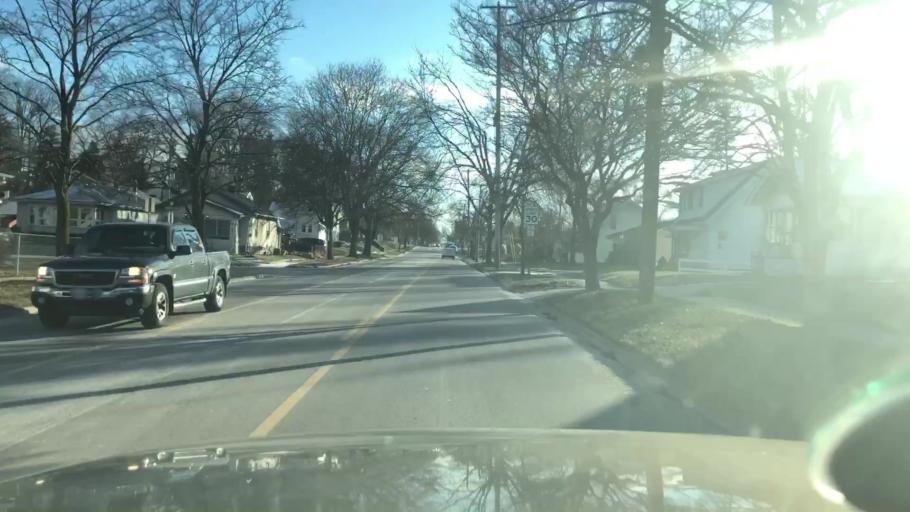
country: US
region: Michigan
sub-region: Jackson County
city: Jackson
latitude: 42.2360
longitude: -84.4233
